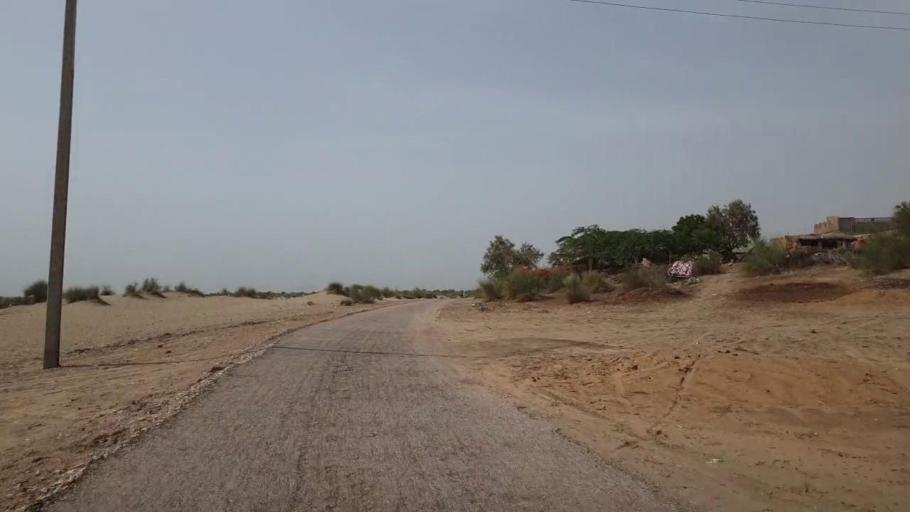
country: PK
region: Sindh
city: Bandhi
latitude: 26.5393
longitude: 68.3867
